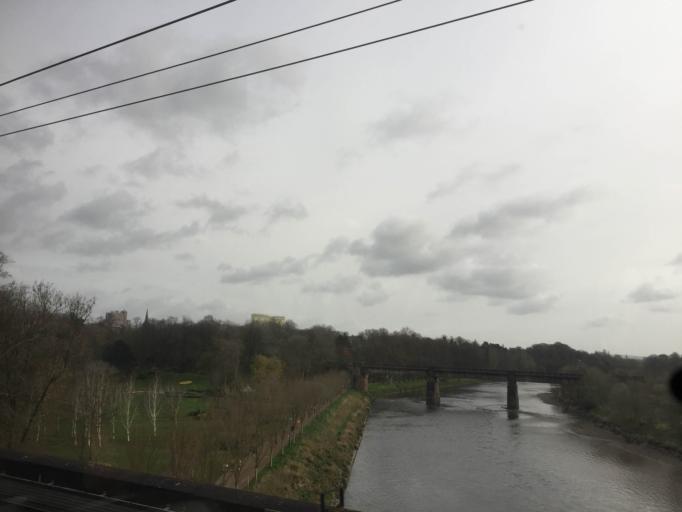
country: GB
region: England
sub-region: Lancashire
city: Preston
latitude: 53.7501
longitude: -2.7061
